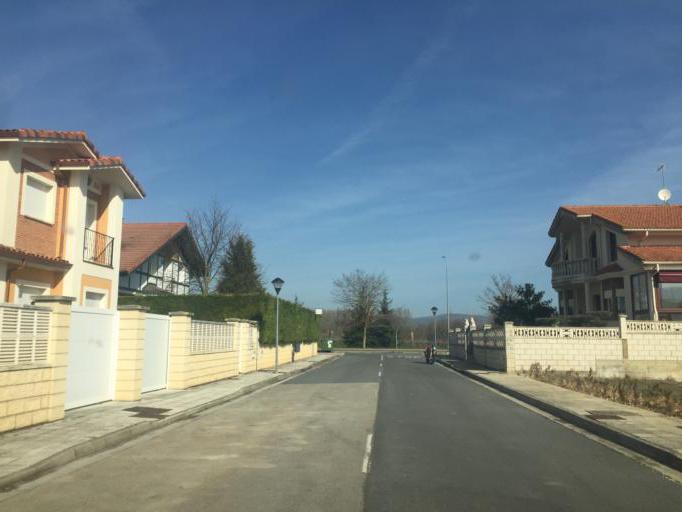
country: ES
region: Castille and Leon
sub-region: Provincia de Burgos
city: Medina de Pomar
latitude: 42.9381
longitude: -3.5830
